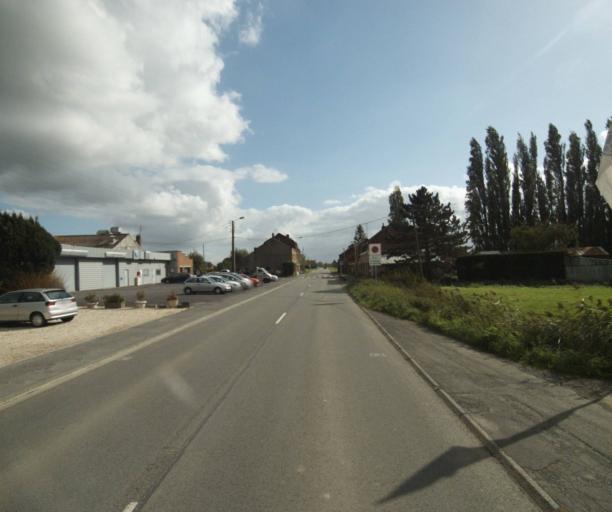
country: FR
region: Nord-Pas-de-Calais
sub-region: Departement du Nord
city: Frelinghien
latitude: 50.7065
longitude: 2.9551
